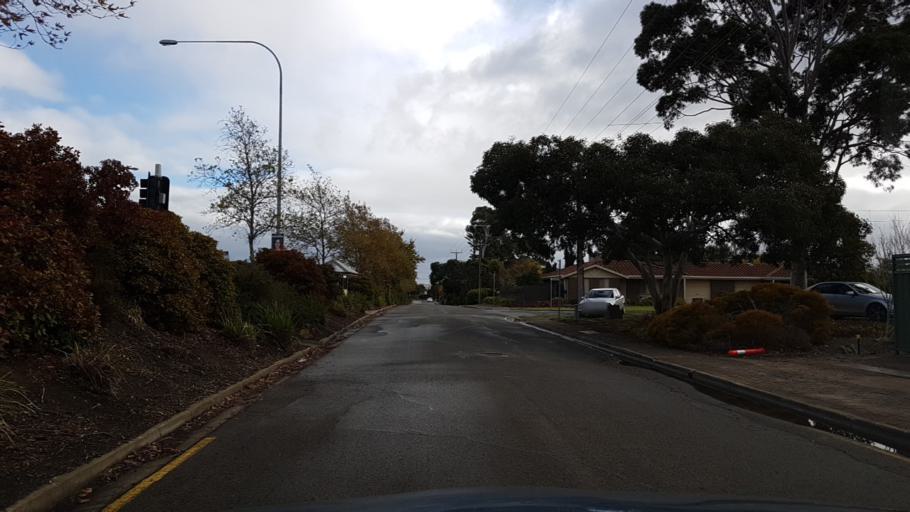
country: AU
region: South Australia
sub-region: Onkaparinga
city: Bedford Park
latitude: -35.0452
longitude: 138.5709
